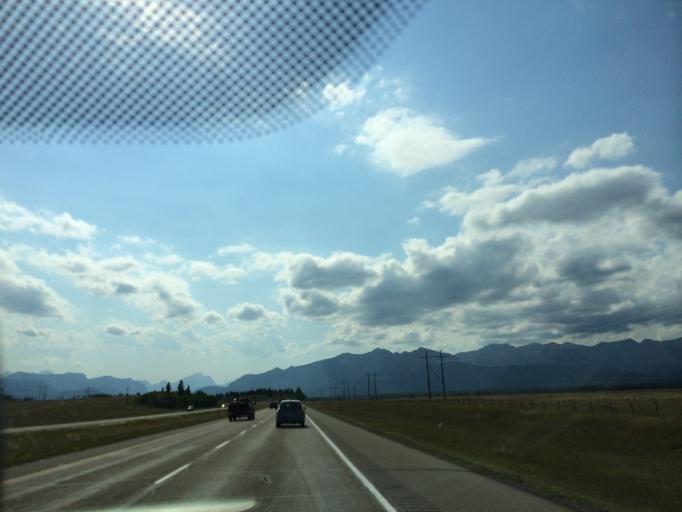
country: CA
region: Alberta
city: Canmore
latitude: 51.1299
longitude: -114.9501
